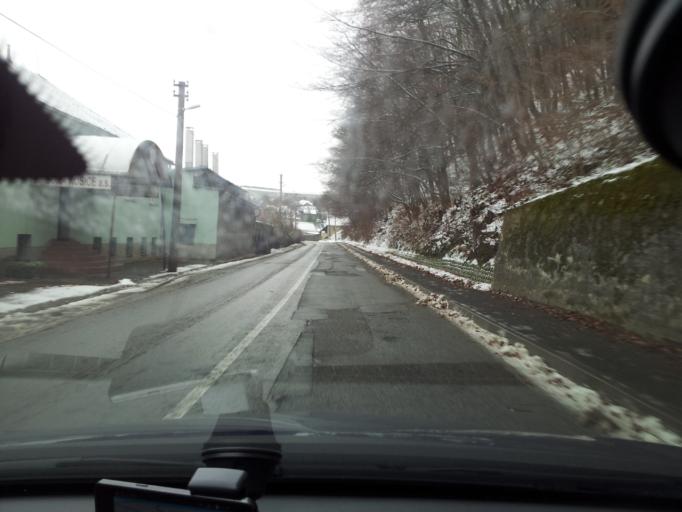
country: SK
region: Presovsky
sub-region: Okres Presov
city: Presov
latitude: 48.8597
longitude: 21.2321
